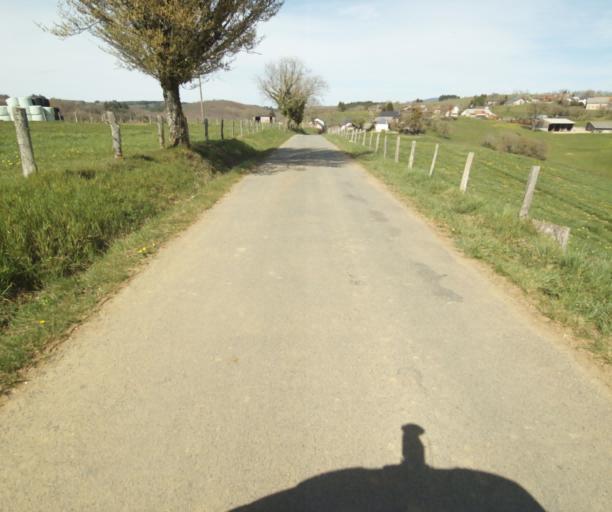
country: FR
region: Limousin
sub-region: Departement de la Correze
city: Seilhac
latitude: 45.3826
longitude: 1.7770
